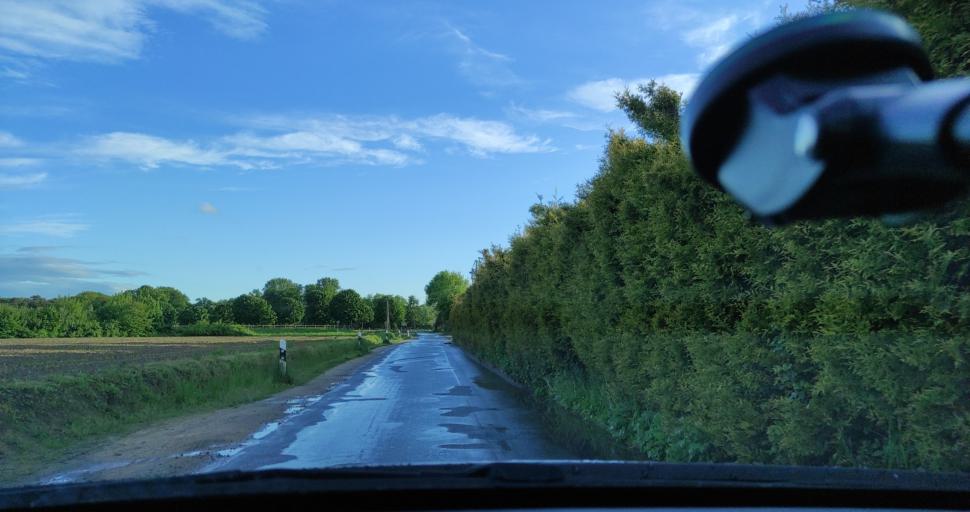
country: DE
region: North Rhine-Westphalia
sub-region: Regierungsbezirk Munster
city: Greven
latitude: 52.0979
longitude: 7.5718
